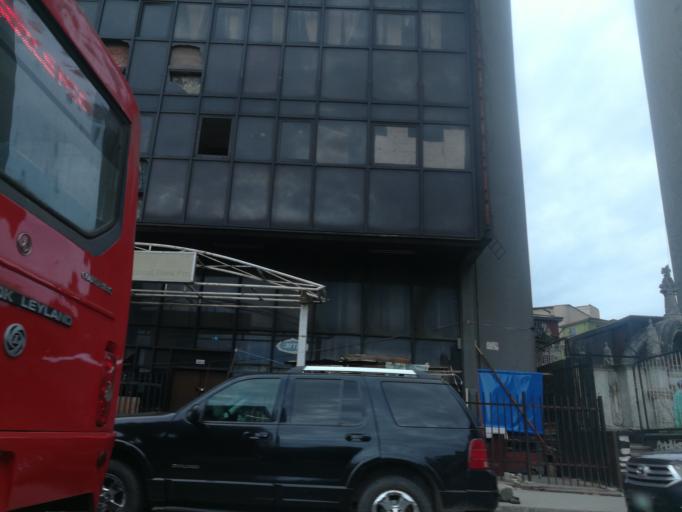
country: NG
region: Lagos
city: Lagos
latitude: 6.4543
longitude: 3.3876
